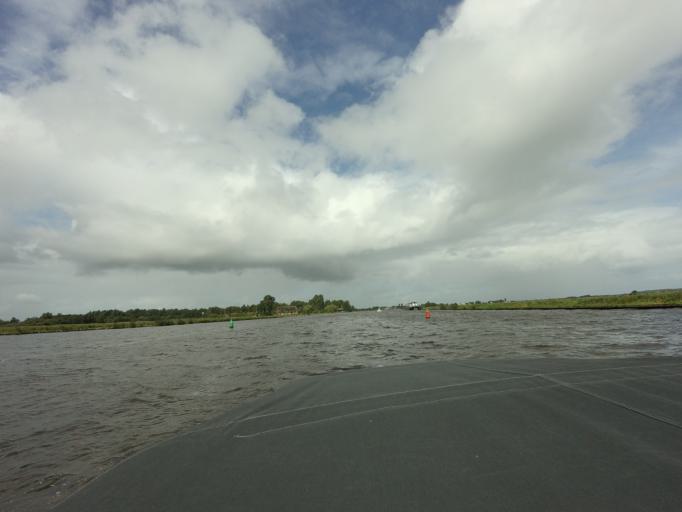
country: NL
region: Friesland
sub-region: Gemeente Boarnsterhim
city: Warten
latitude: 53.1363
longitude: 5.9173
